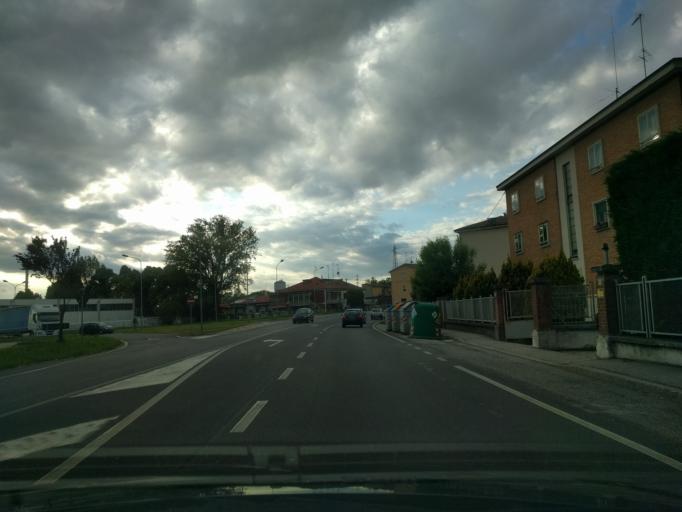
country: IT
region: Veneto
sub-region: Provincia di Rovigo
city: Santa Maria Maddalena
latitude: 44.8844
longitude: 11.6082
